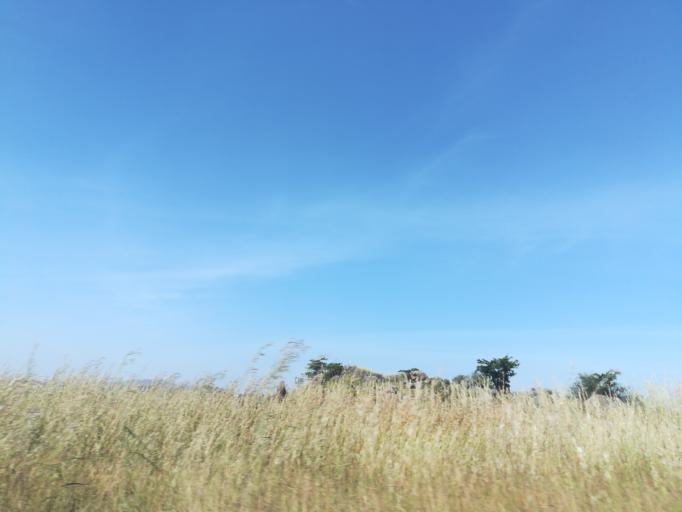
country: NG
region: Plateau
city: Bukuru
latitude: 9.7492
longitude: 8.9084
